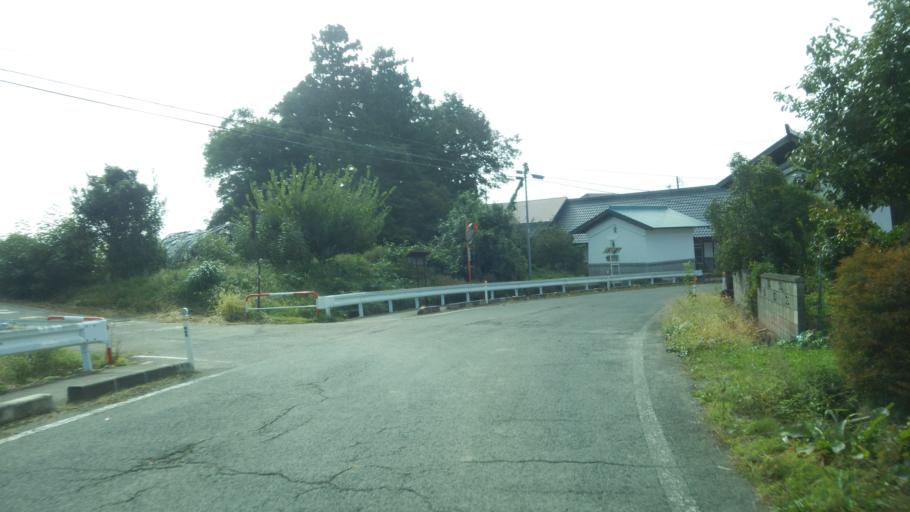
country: JP
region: Fukushima
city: Kitakata
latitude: 37.5804
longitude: 139.9465
